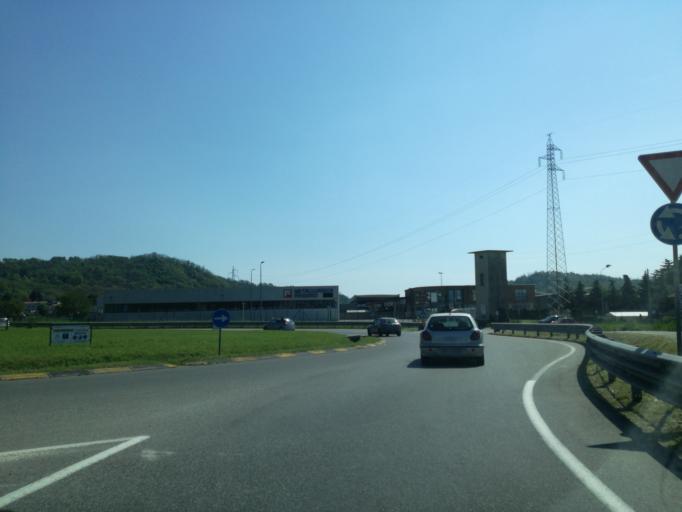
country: IT
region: Lombardy
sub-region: Provincia di Bergamo
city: Villa d'Adda
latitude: 45.7130
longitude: 9.4569
